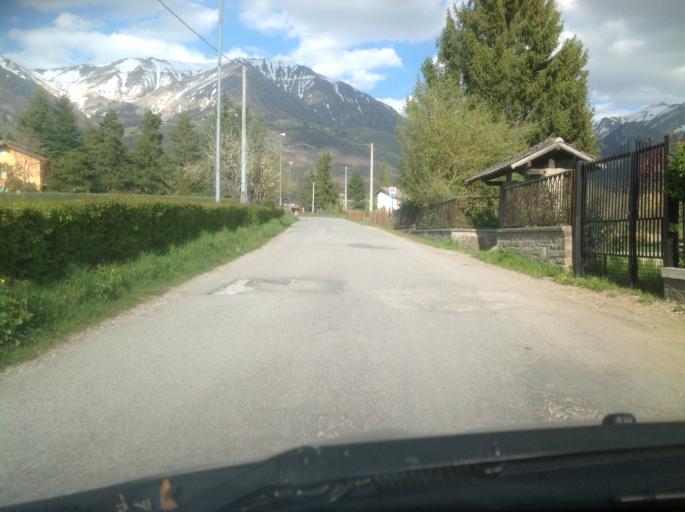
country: IT
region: Latium
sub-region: Provincia di Rieti
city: Amatrice
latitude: 42.6345
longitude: 13.3043
